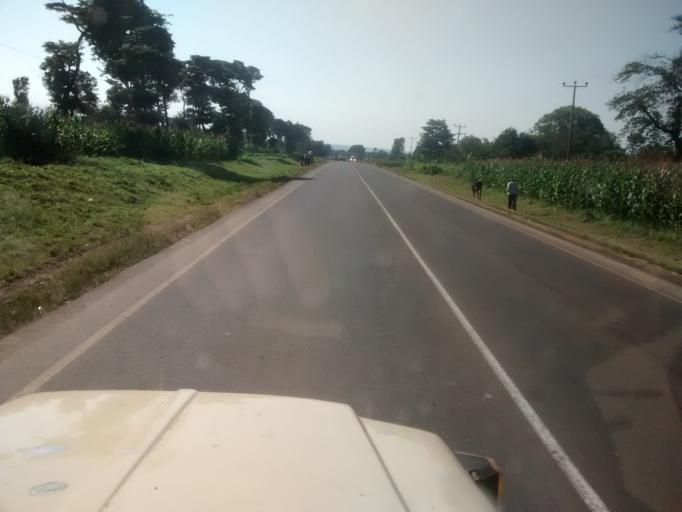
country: TZ
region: Arusha
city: Nkoaranga
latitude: -3.3714
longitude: 36.8035
